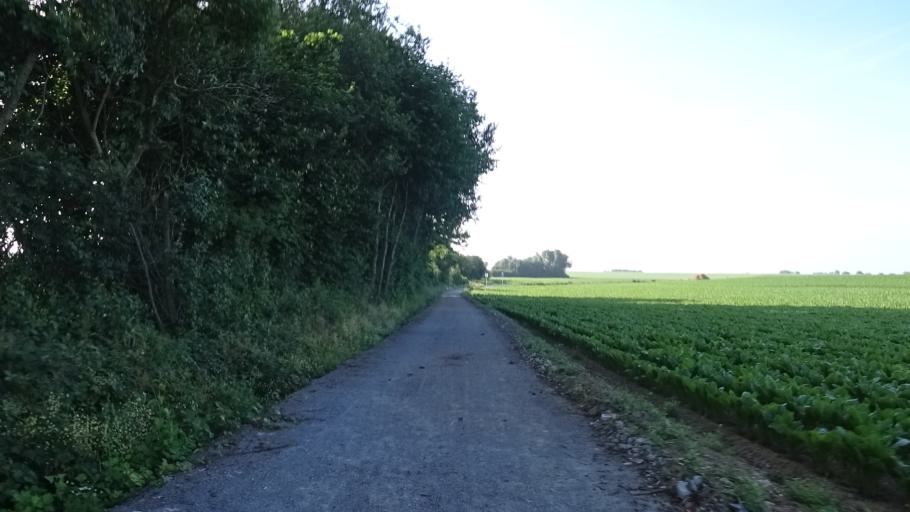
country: BE
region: Wallonia
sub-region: Province du Brabant Wallon
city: Walhain-Saint-Paul
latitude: 50.6093
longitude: 4.7141
